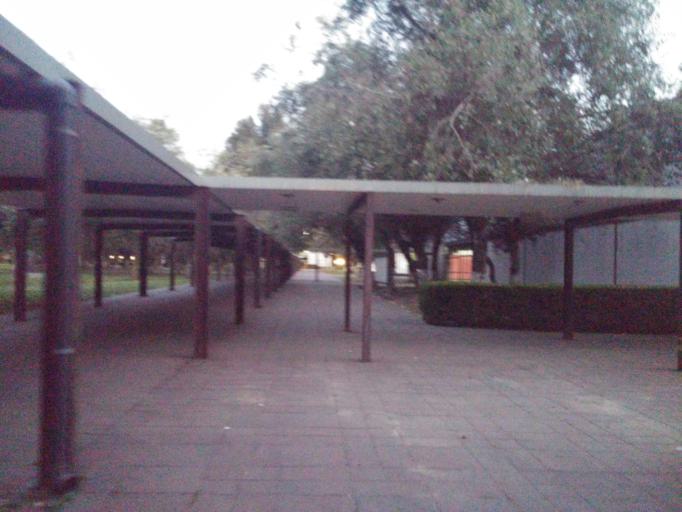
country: MX
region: Mexico
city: Colonia Lindavista
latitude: 19.4968
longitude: -99.1355
